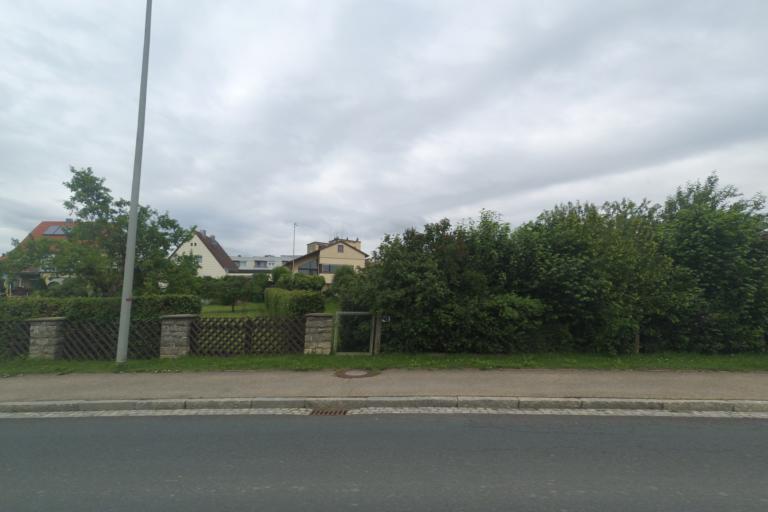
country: DE
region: Bavaria
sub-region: Regierungsbezirk Mittelfranken
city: Uffenheim
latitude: 49.5485
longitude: 10.2420
